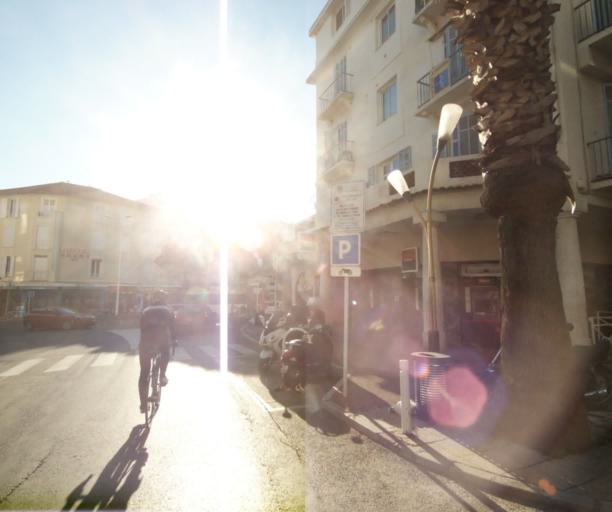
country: FR
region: Provence-Alpes-Cote d'Azur
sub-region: Departement des Alpes-Maritimes
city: Antibes
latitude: 43.5686
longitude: 7.1128
